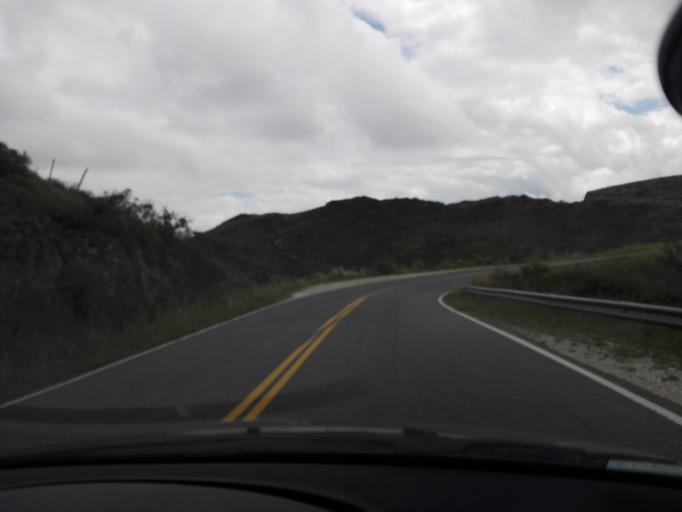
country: AR
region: Cordoba
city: Cuesta Blanca
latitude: -31.5950
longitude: -64.5385
